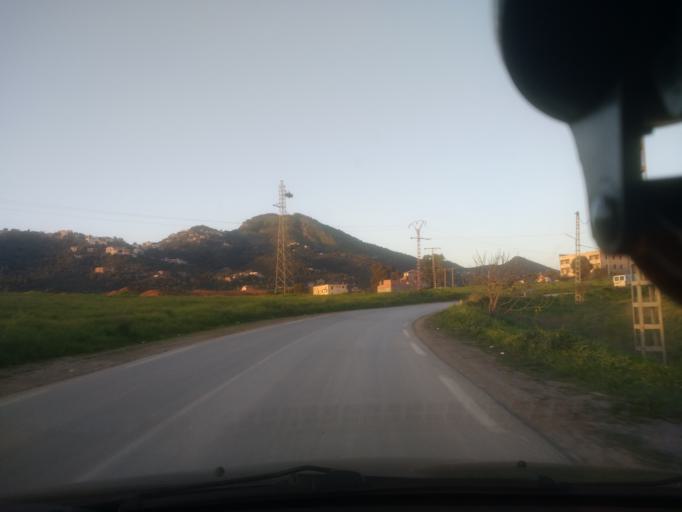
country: DZ
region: Boumerdes
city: Makouda
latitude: 36.7735
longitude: 4.0632
